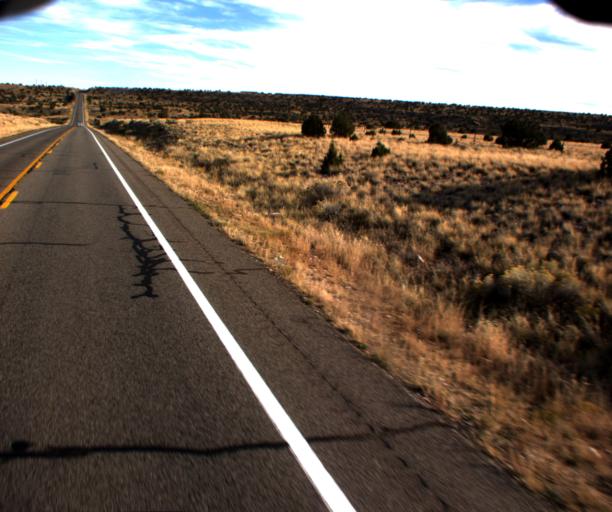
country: US
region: New Mexico
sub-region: San Juan County
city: Shiprock
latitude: 36.8884
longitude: -109.0577
